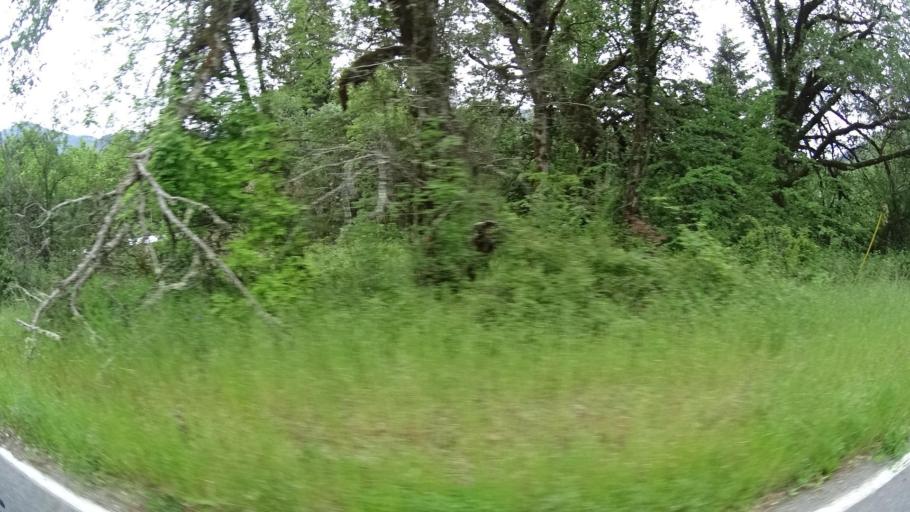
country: US
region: California
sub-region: Humboldt County
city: Willow Creek
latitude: 41.0946
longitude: -123.7119
